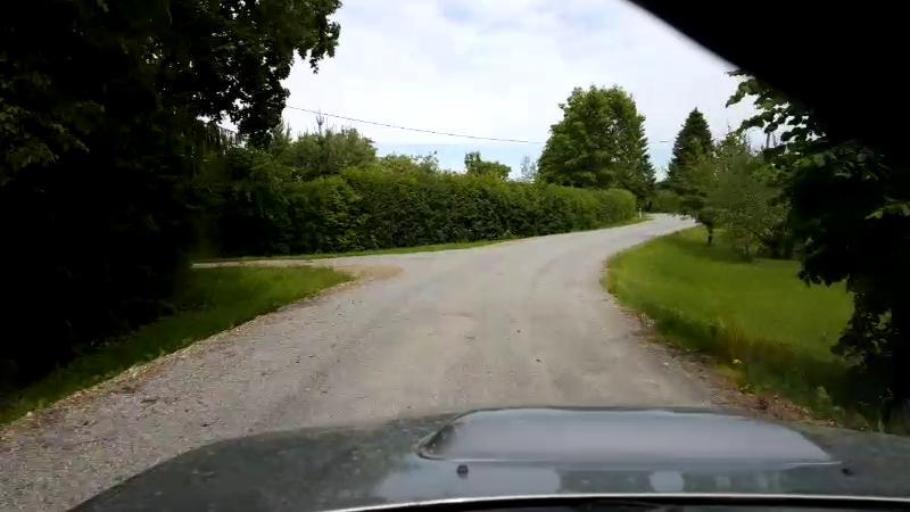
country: EE
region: Paernumaa
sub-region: Tootsi vald
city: Tootsi
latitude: 58.5390
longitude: 24.7348
